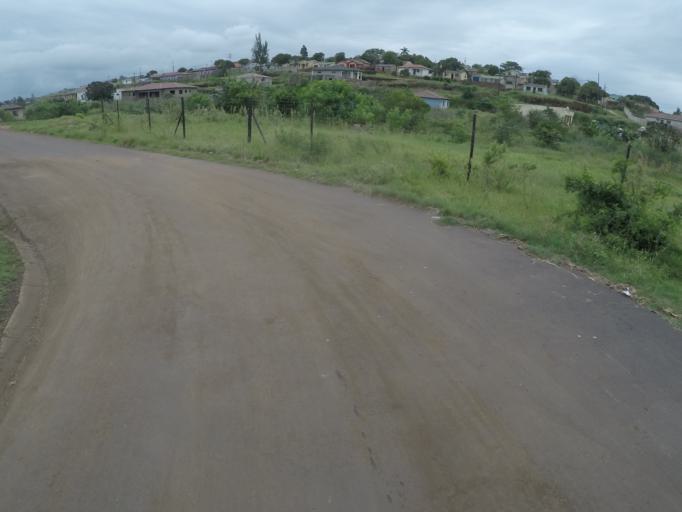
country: ZA
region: KwaZulu-Natal
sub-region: uThungulu District Municipality
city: Empangeni
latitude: -28.7769
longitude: 31.8570
